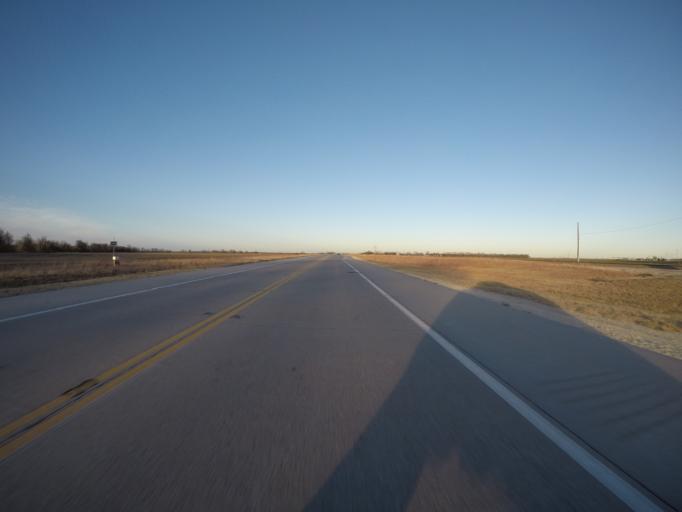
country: US
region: Kansas
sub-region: Harvey County
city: North Newton
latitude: 38.0866
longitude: -97.2897
